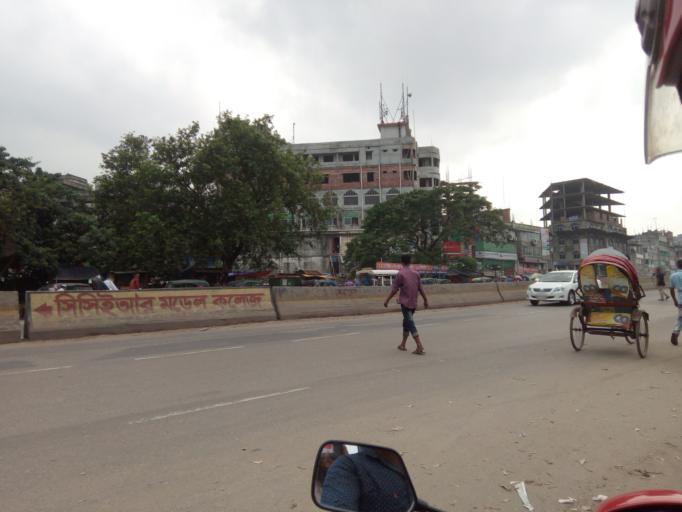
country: BD
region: Dhaka
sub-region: Dhaka
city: Dhaka
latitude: 23.7025
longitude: 90.4514
